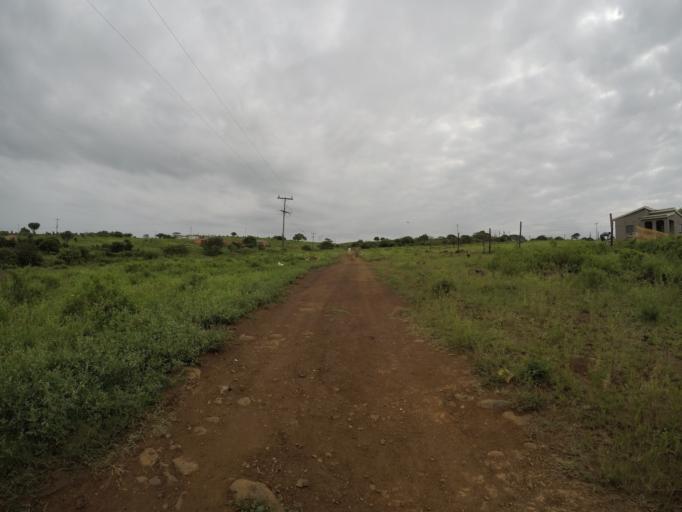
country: ZA
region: KwaZulu-Natal
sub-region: uThungulu District Municipality
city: Empangeni
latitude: -28.6401
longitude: 31.9053
